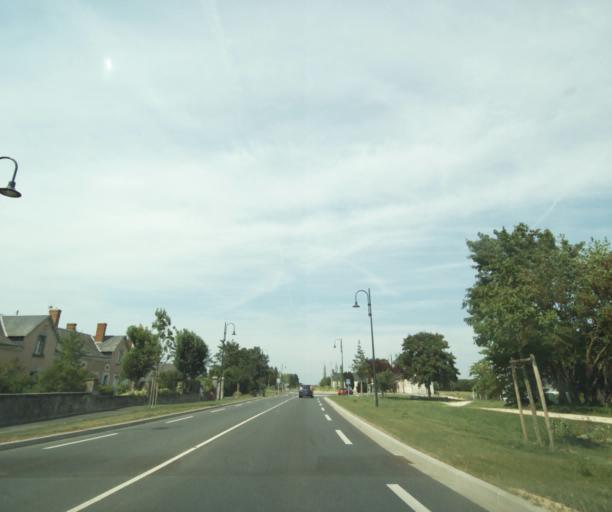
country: FR
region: Centre
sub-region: Departement d'Indre-et-Loire
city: Sorigny
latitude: 47.2457
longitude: 0.6959
